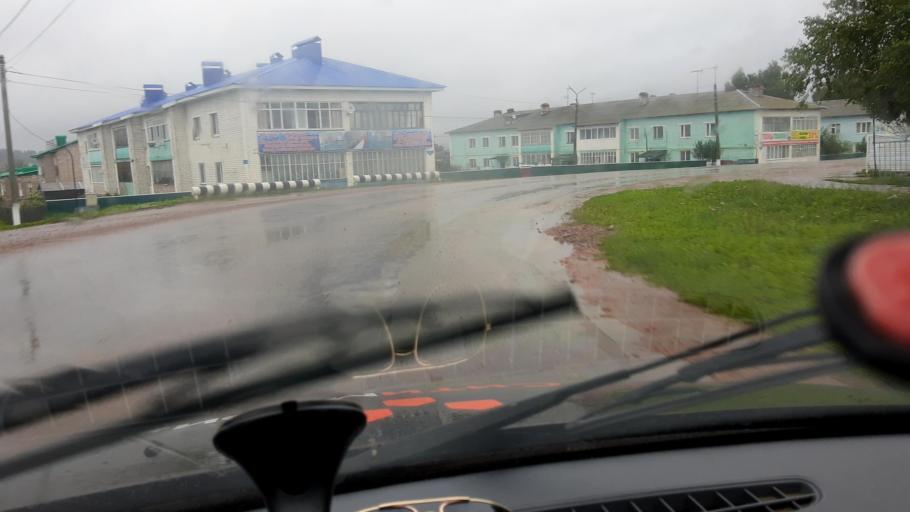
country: RU
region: Bashkortostan
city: Karmaskaly
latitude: 53.8917
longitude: 56.4627
